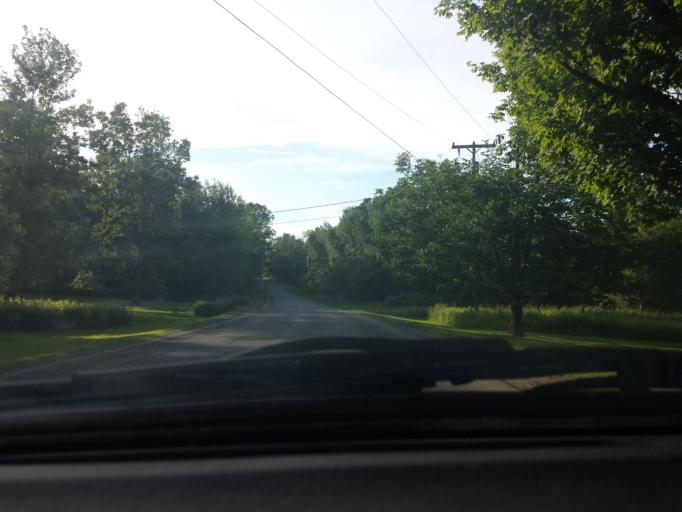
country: US
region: New York
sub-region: St. Lawrence County
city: Potsdam
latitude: 44.6923
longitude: -74.9650
